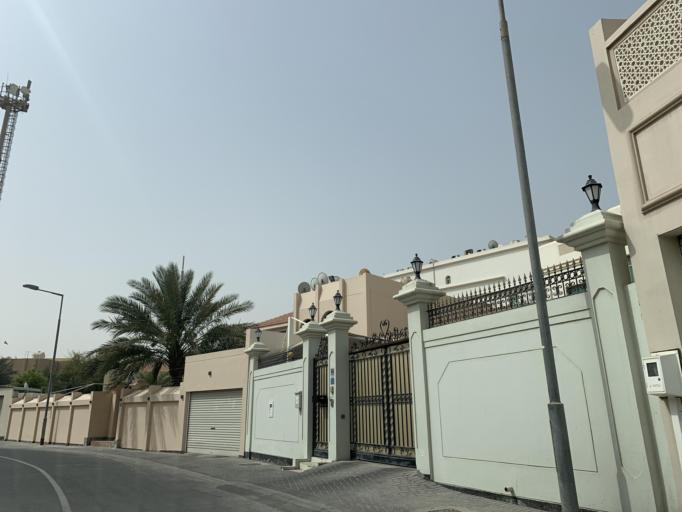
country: BH
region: Northern
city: Madinat `Isa
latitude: 26.1671
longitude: 50.5541
